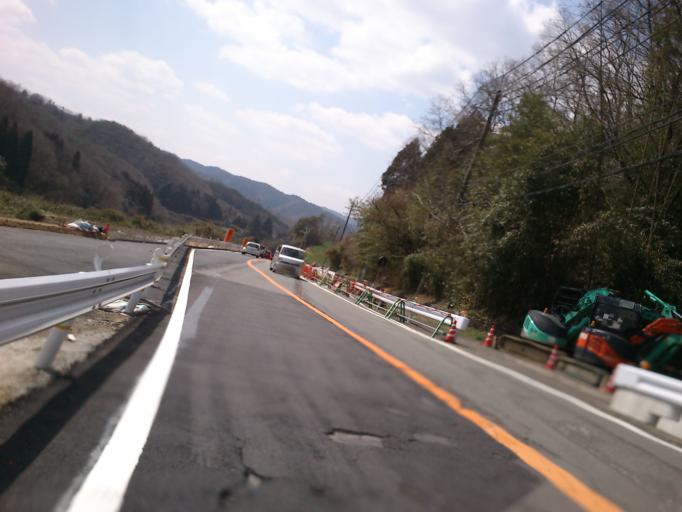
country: JP
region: Mie
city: Ueno-ebisumachi
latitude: 34.7772
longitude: 136.0116
